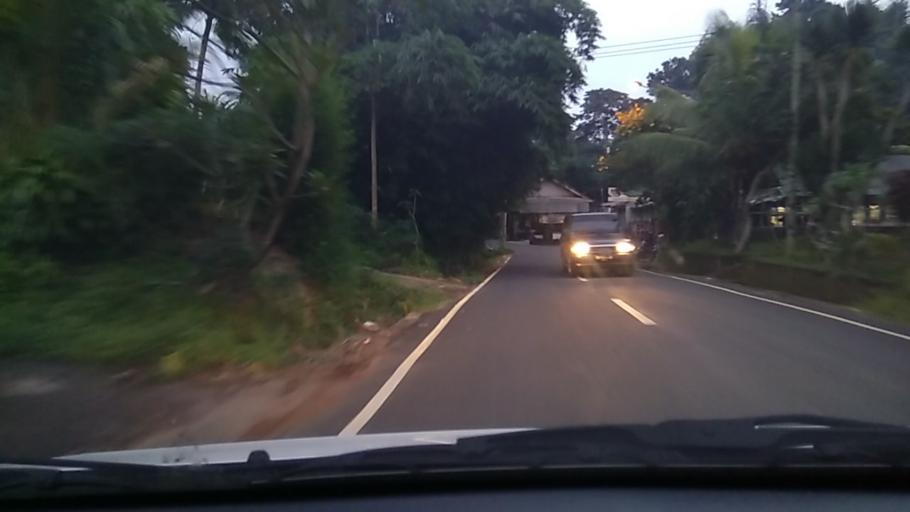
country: ID
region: Bali
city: Basa
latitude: -8.4730
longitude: 115.1841
